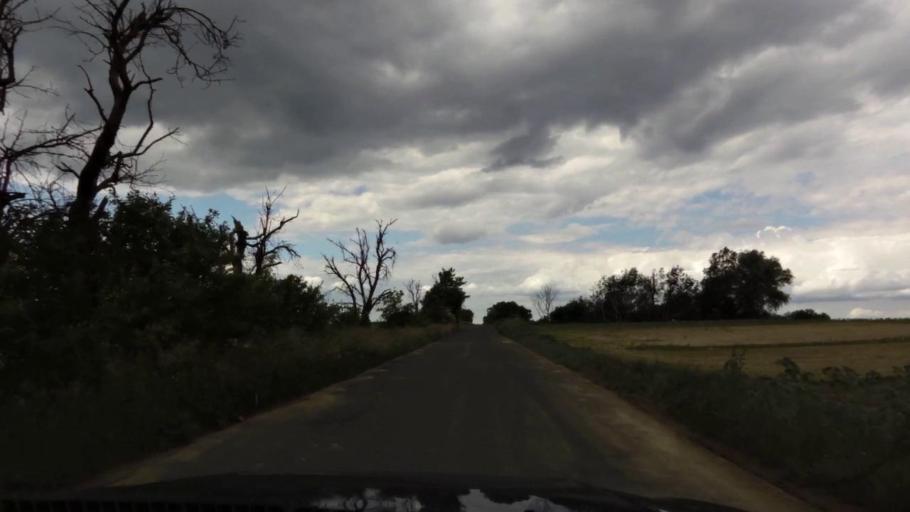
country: PL
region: West Pomeranian Voivodeship
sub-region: Powiat mysliborski
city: Mysliborz
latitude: 52.9791
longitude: 14.7862
